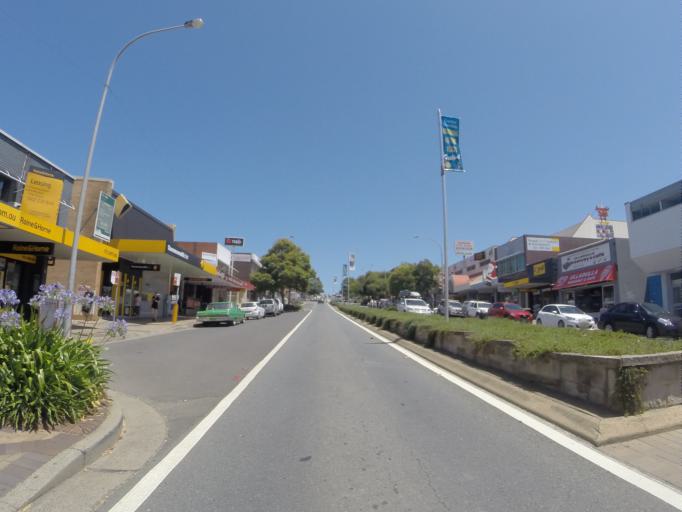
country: AU
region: New South Wales
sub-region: Shoalhaven Shire
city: Ulladulla
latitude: -35.3570
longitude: 150.4744
